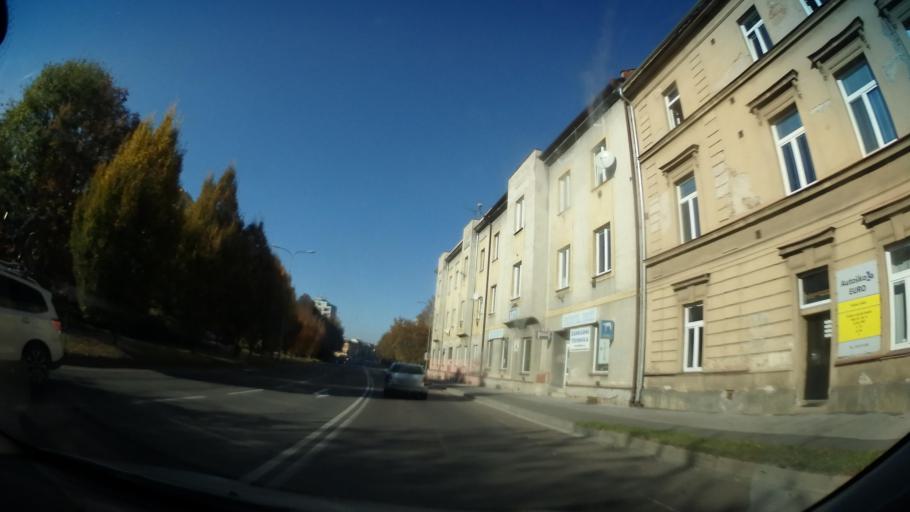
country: CZ
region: Pardubicky
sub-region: Okres Chrudim
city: Chrudim
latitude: 49.9454
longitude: 15.7949
